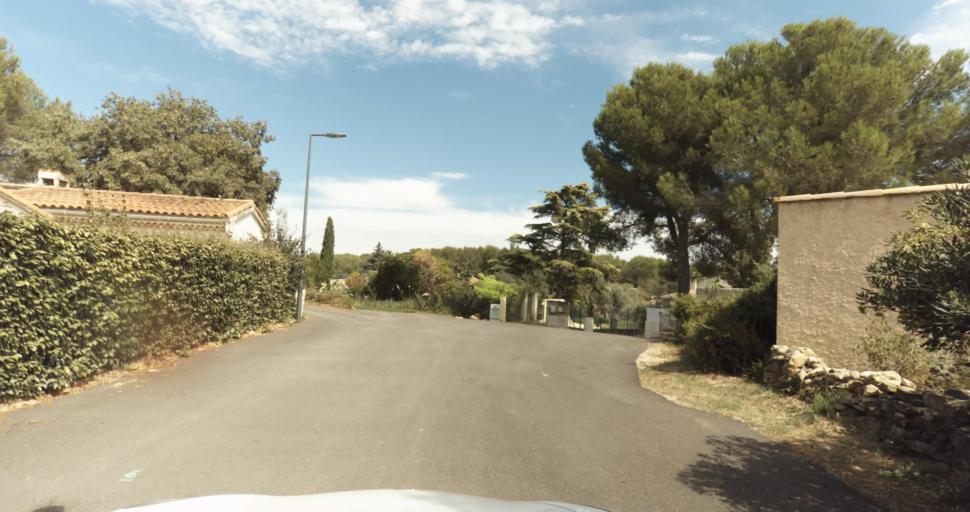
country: FR
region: Provence-Alpes-Cote d'Azur
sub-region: Departement des Bouches-du-Rhone
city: Miramas
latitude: 43.5819
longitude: 5.0231
